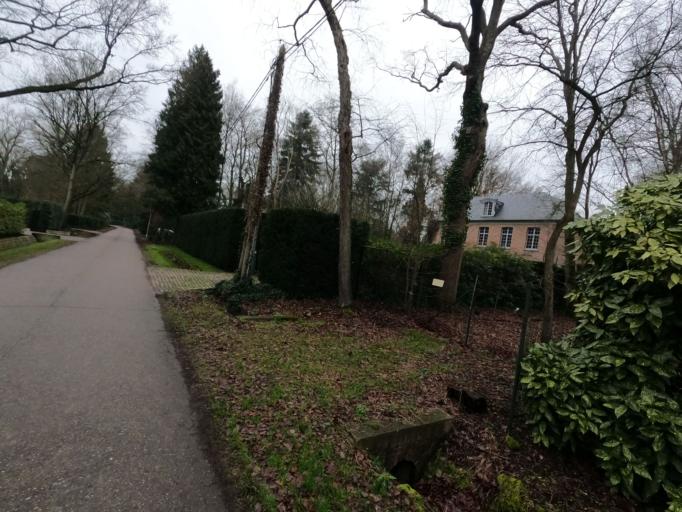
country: BE
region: Flanders
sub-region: Provincie Antwerpen
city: Schilde
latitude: 51.2760
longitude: 4.6194
